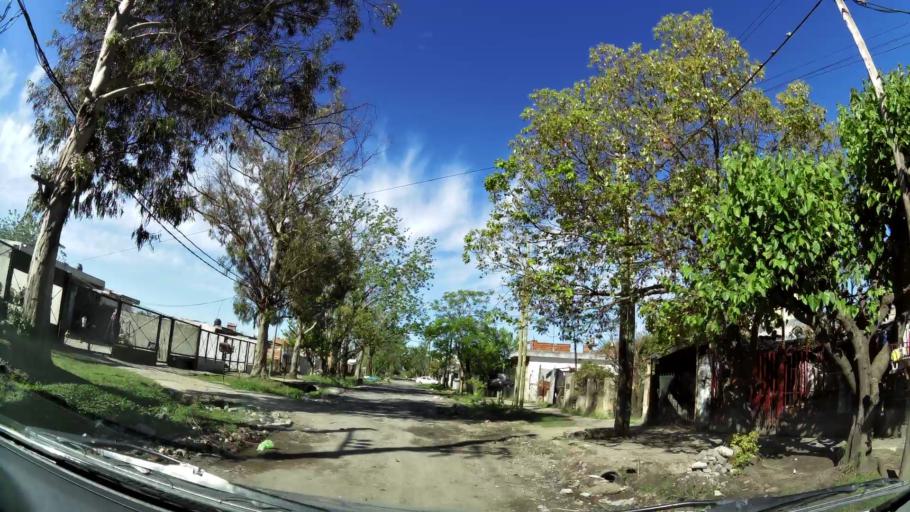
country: AR
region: Buenos Aires
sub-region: Partido de Quilmes
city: Quilmes
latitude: -34.7633
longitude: -58.3096
